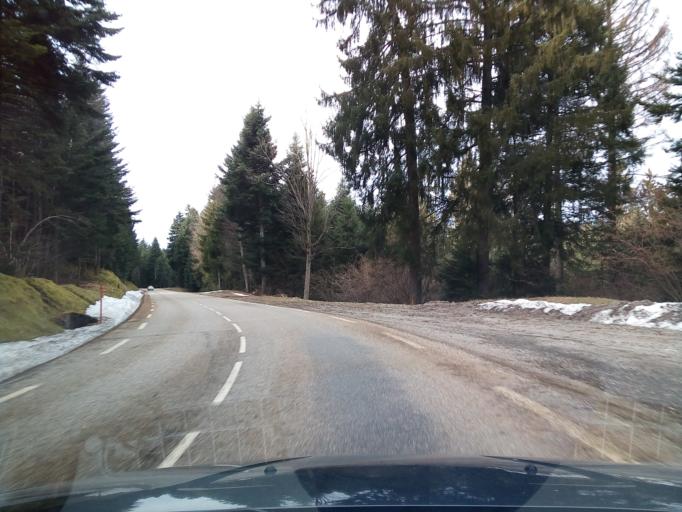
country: FR
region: Rhone-Alpes
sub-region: Departement de l'Isere
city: Revel
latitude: 45.1542
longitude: 5.8798
